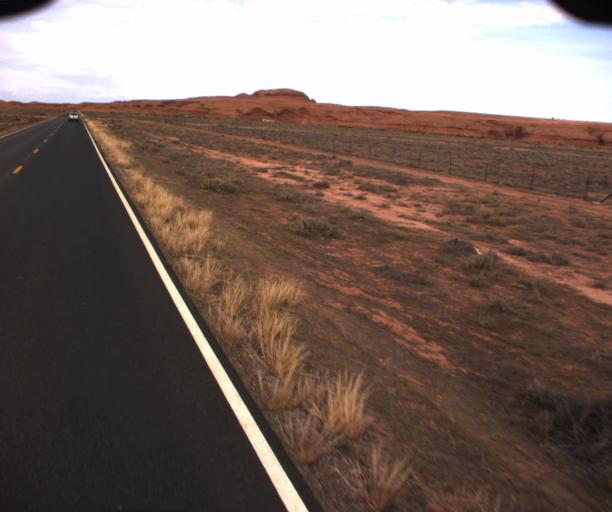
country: US
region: Arizona
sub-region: Apache County
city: Many Farms
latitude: 36.7512
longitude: -109.6437
